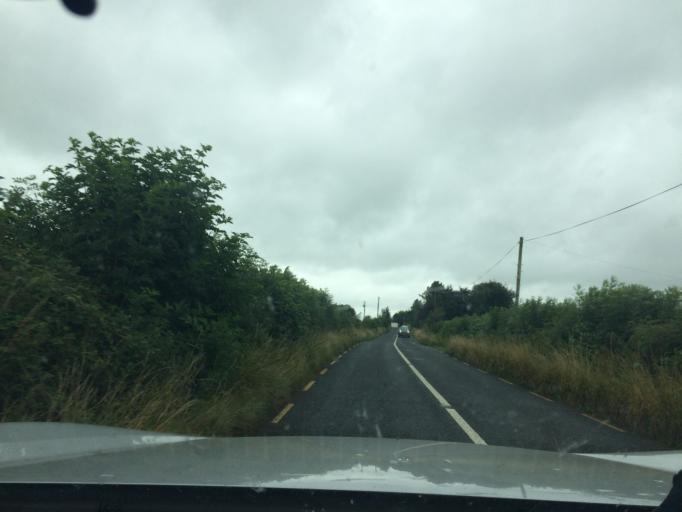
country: IE
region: Munster
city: Cashel
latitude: 52.6111
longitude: -7.8806
